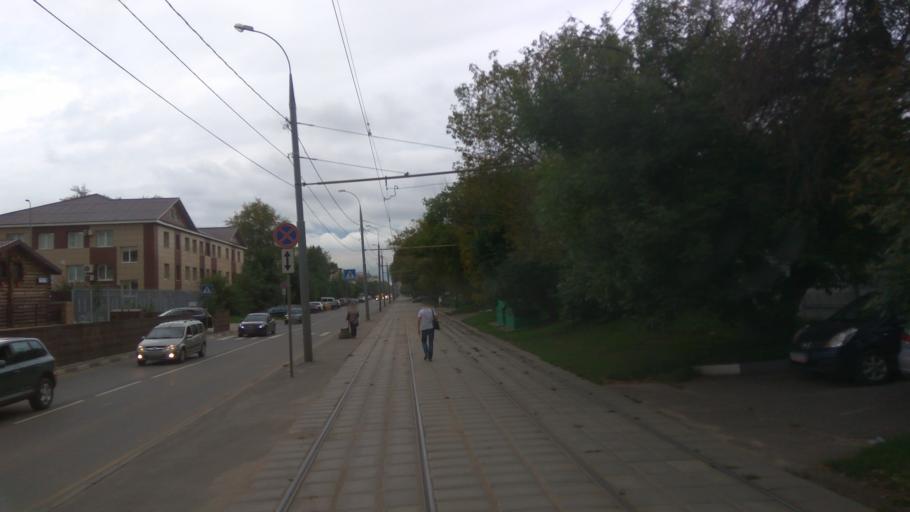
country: RU
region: Moskovskaya
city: Kozhukhovo
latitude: 55.7147
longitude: 37.6930
